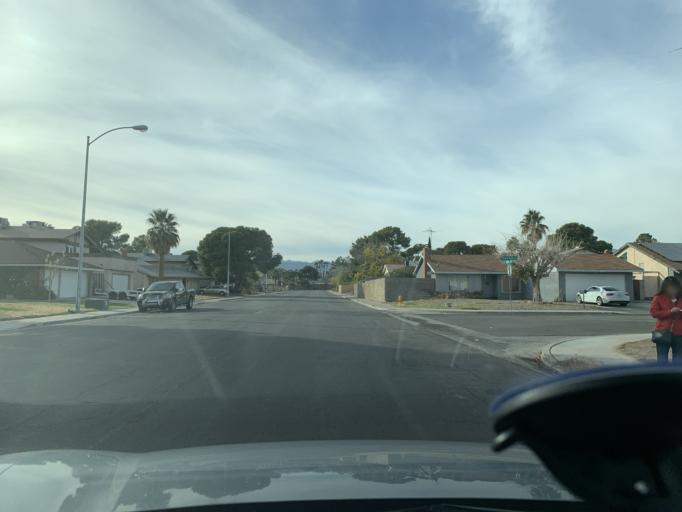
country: US
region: Nevada
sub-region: Clark County
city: Spring Valley
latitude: 36.1092
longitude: -115.2352
